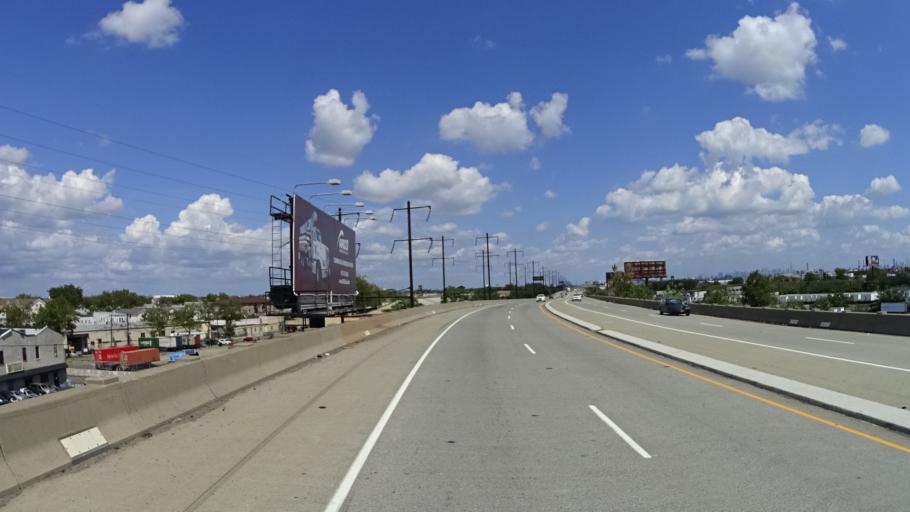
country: US
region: New Jersey
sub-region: Essex County
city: Newark
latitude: 40.7183
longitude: -74.1544
